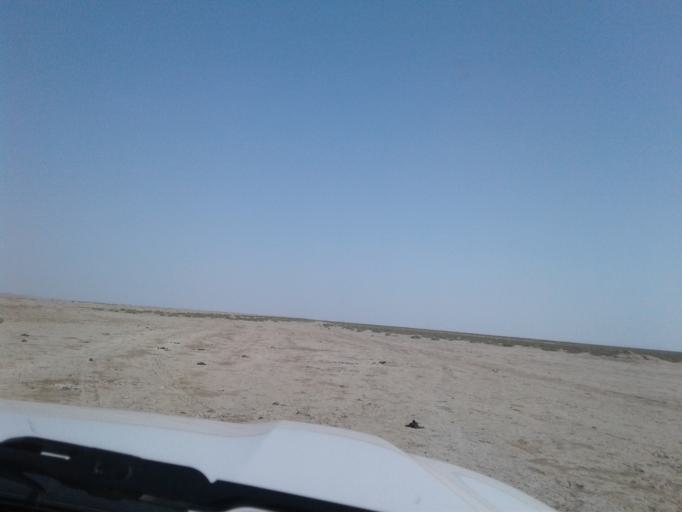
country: TM
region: Balkan
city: Gumdag
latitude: 38.3587
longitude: 54.5234
